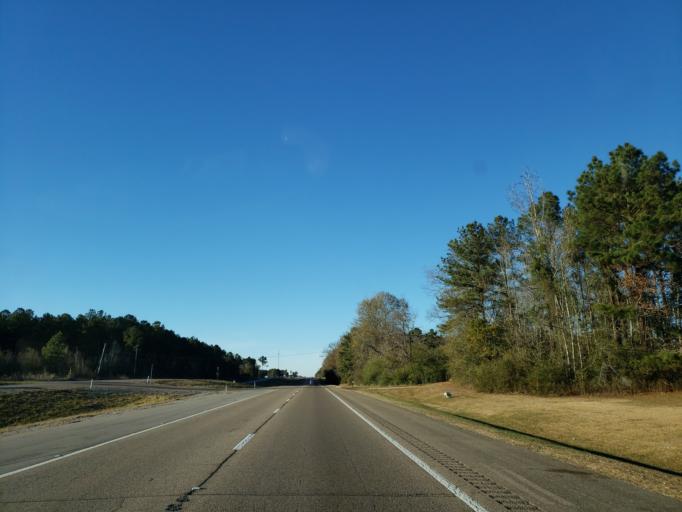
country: US
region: Mississippi
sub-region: Lamar County
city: Sumrall
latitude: 31.4848
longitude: -89.4641
